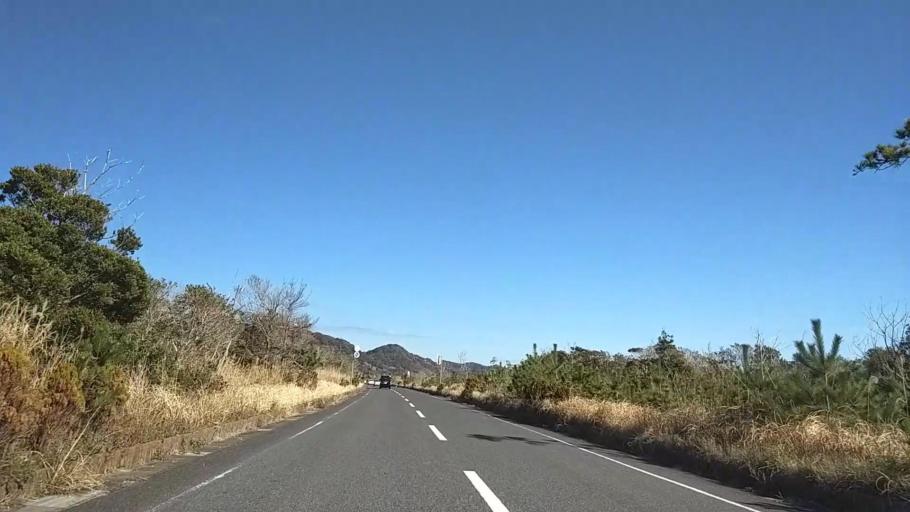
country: JP
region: Chiba
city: Tateyama
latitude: 35.0189
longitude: 139.9872
